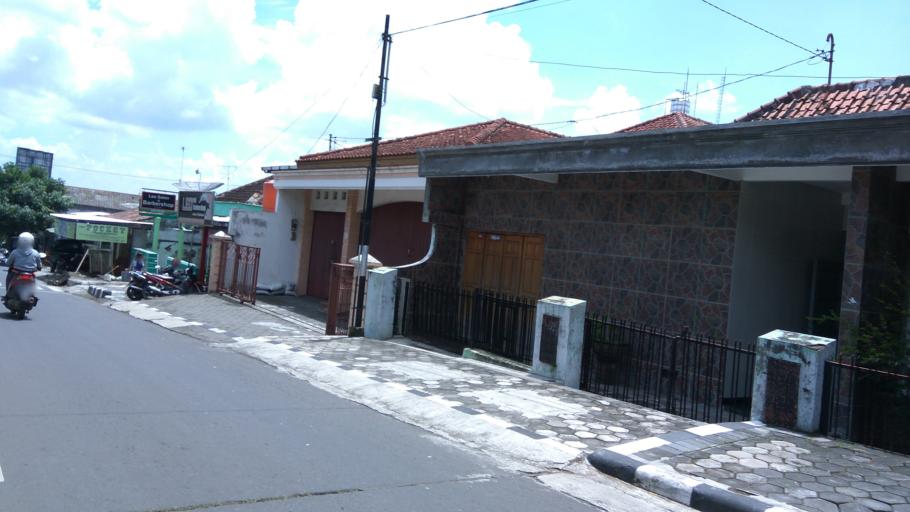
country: ID
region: Central Java
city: Ambarawa
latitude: -7.2559
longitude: 110.4051
